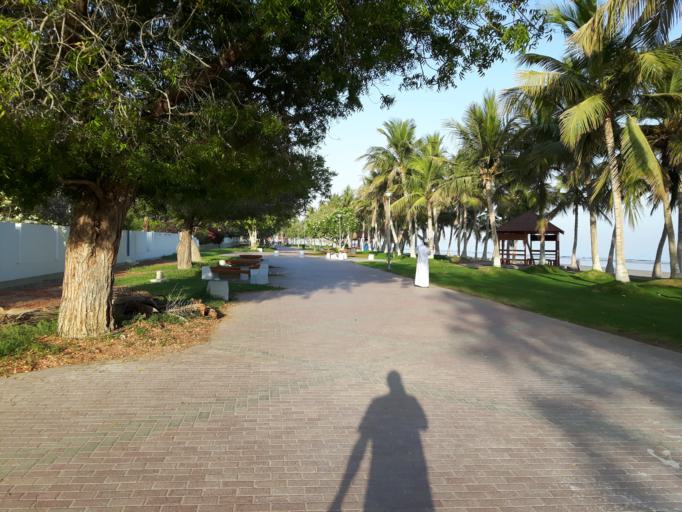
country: OM
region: Muhafazat Masqat
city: Bawshar
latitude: 23.6158
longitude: 58.4608
